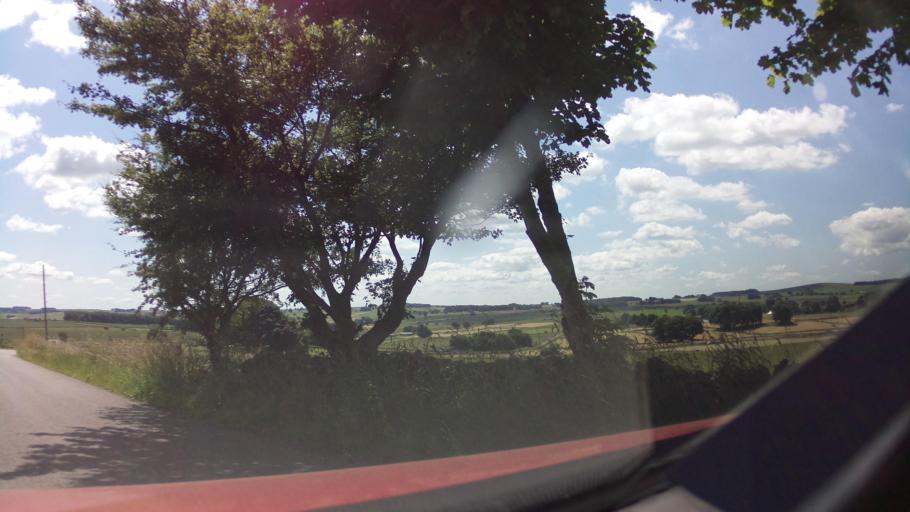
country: GB
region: England
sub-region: Derbyshire
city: Tideswell
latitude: 53.2199
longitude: -1.7783
